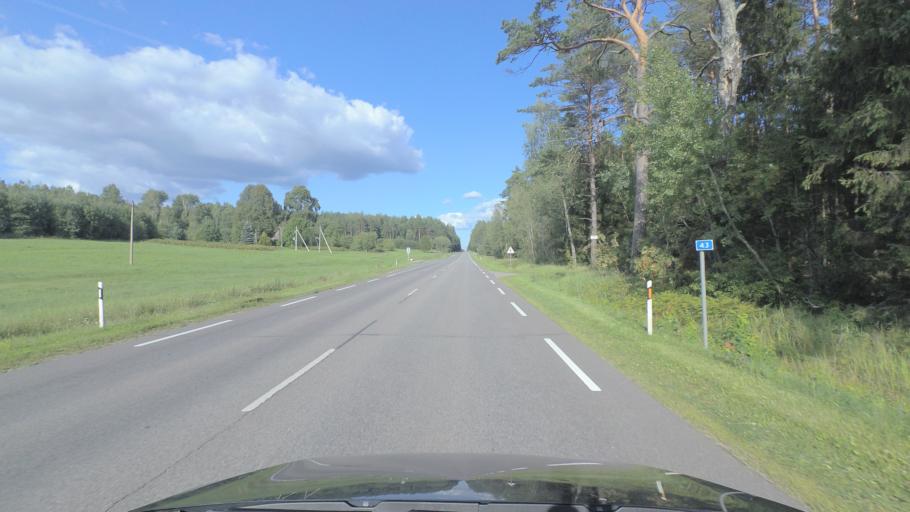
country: LT
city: Pabrade
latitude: 54.9631
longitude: 25.7032
